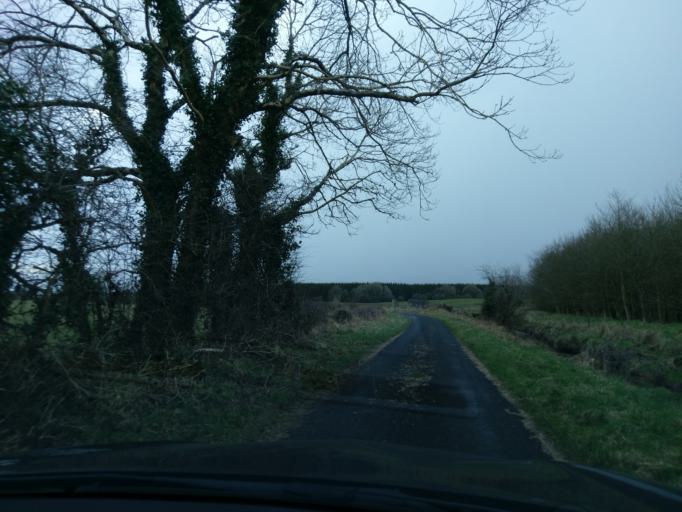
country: IE
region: Connaught
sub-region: County Galway
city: Athenry
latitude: 53.3964
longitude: -8.6131
